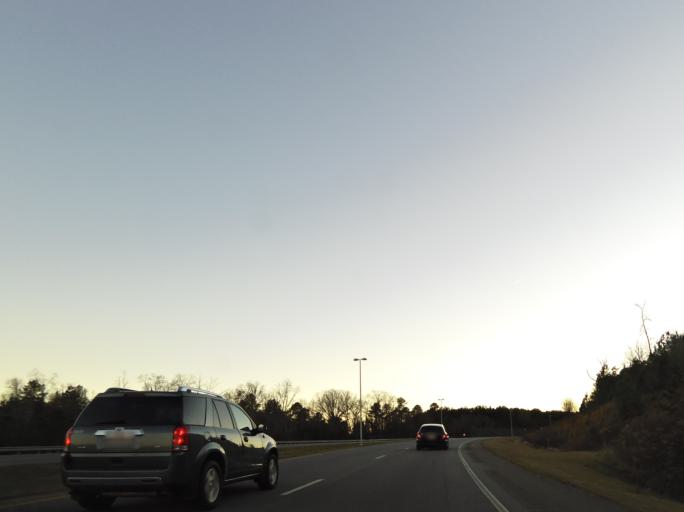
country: US
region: Georgia
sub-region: Houston County
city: Centerville
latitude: 32.5848
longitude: -83.6844
